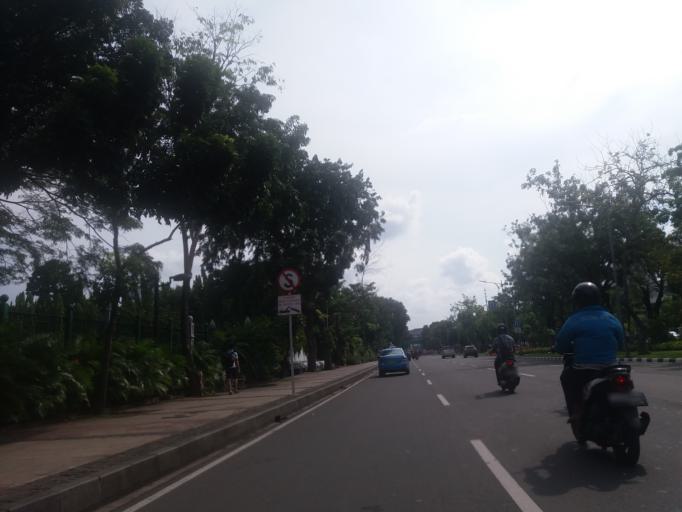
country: ID
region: Jakarta Raya
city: Jakarta
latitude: -6.1715
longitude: 106.8276
